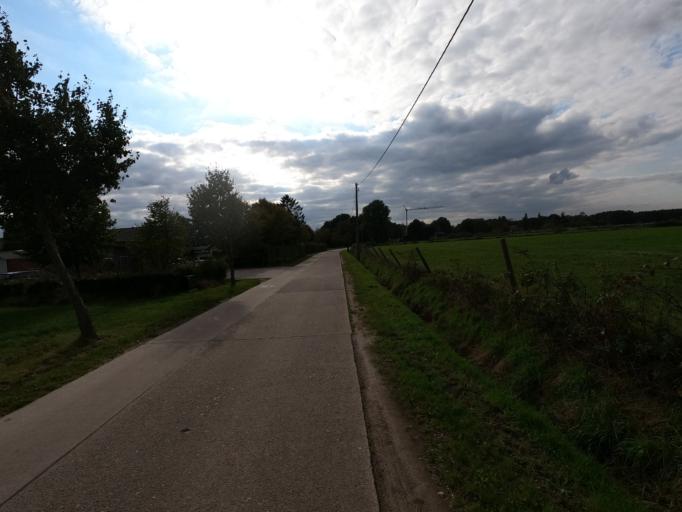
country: BE
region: Flanders
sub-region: Provincie Antwerpen
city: Kasterlee
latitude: 51.2092
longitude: 4.9246
